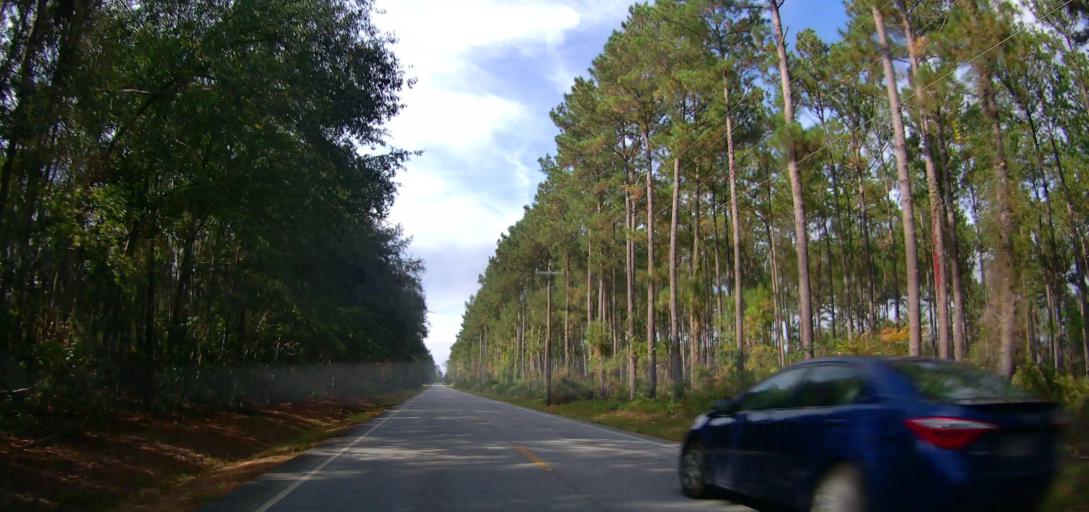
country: US
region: Georgia
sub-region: Thomas County
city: Thomasville
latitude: 30.9260
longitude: -84.0176
